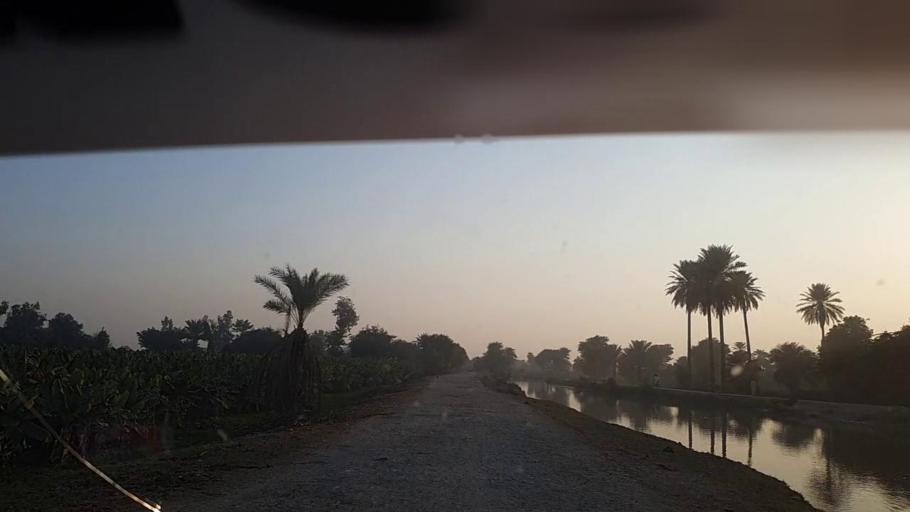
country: PK
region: Sindh
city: Ranipur
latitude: 27.2335
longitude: 68.5487
